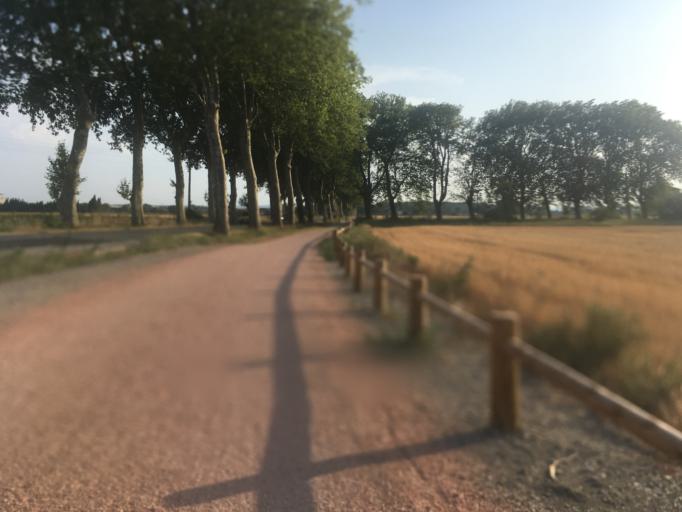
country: FR
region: Languedoc-Roussillon
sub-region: Departement de l'Aude
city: Bram
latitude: 43.2531
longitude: 2.1252
